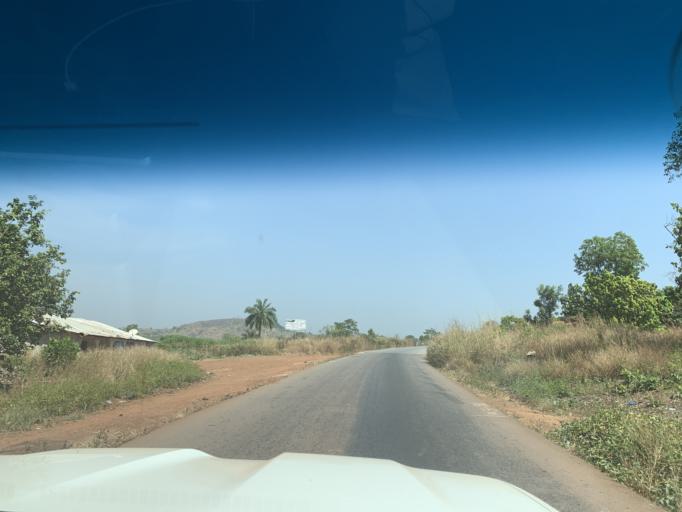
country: GN
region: Kindia
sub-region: Kindia
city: Kindia
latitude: 10.0123
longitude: -12.6899
